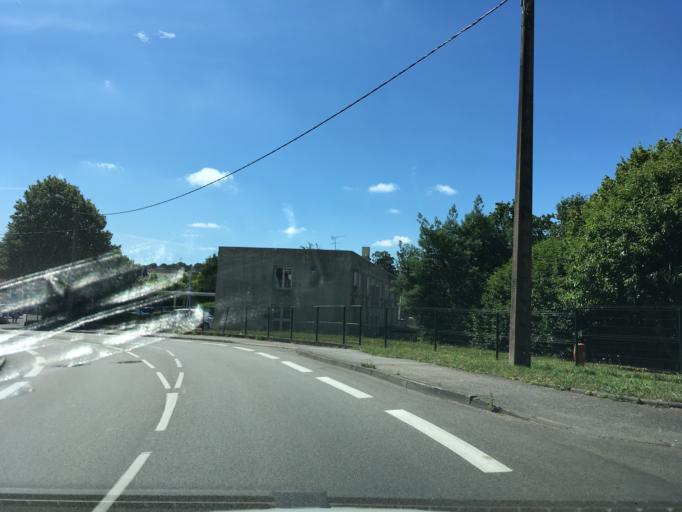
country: FR
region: Brittany
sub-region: Departement du Finistere
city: Quimper
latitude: 47.9969
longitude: -4.0843
